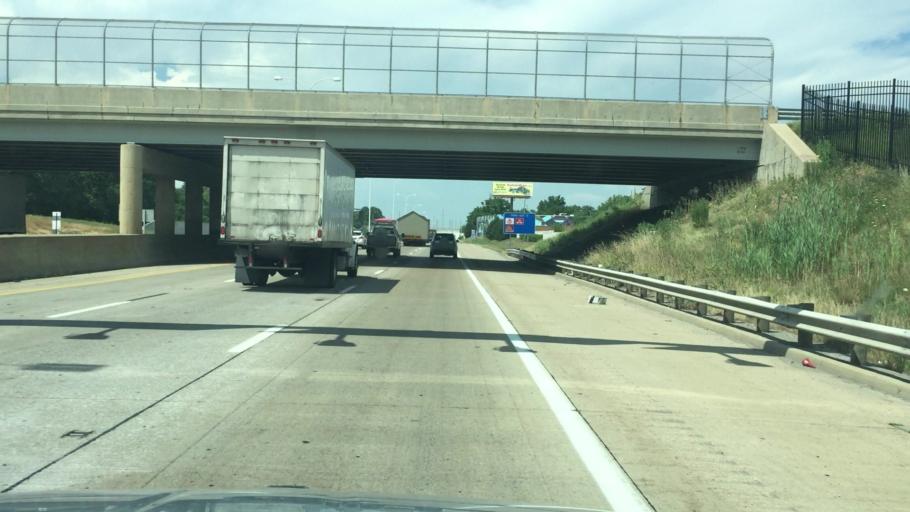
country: US
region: Ohio
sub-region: Lucas County
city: Toledo
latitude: 41.6788
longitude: -83.5155
